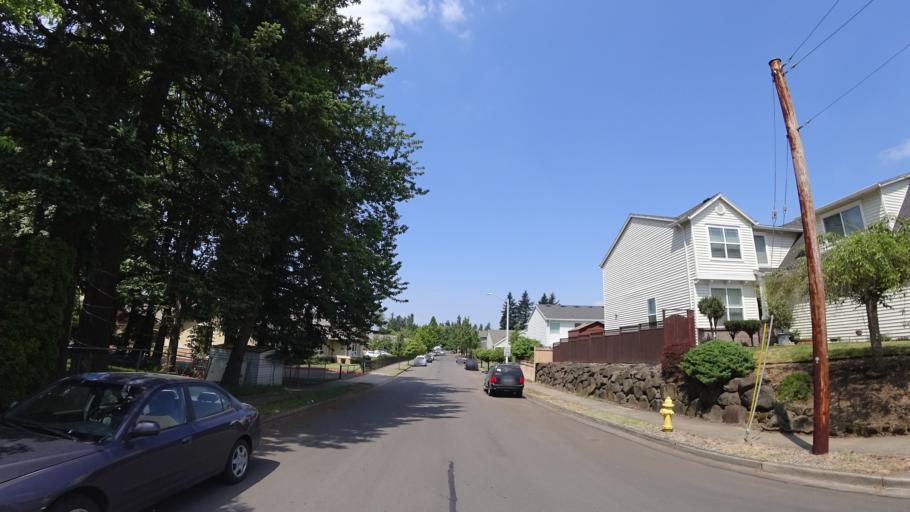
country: US
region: Oregon
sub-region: Multnomah County
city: Fairview
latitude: 45.5284
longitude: -122.4933
